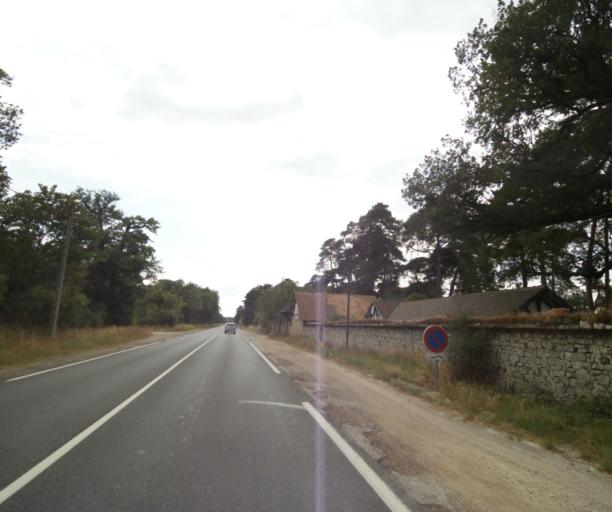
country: FR
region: Ile-de-France
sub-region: Departement de Seine-et-Marne
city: Fontainebleau
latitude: 48.3937
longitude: 2.6828
